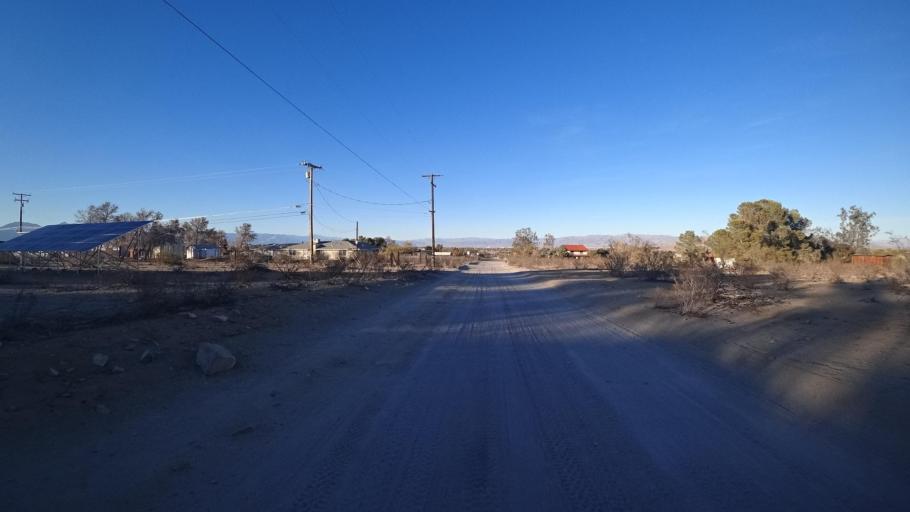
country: US
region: California
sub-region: Kern County
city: Ridgecrest
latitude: 35.5849
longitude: -117.6617
